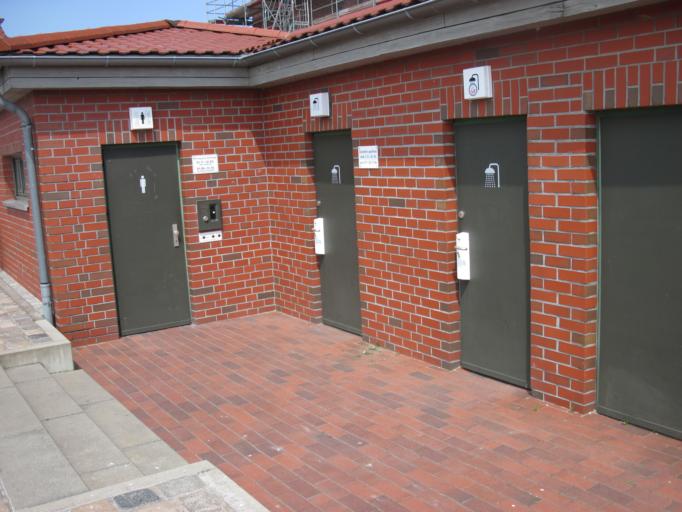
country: DE
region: Mecklenburg-Vorpommern
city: Wismar
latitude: 53.8986
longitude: 11.4585
